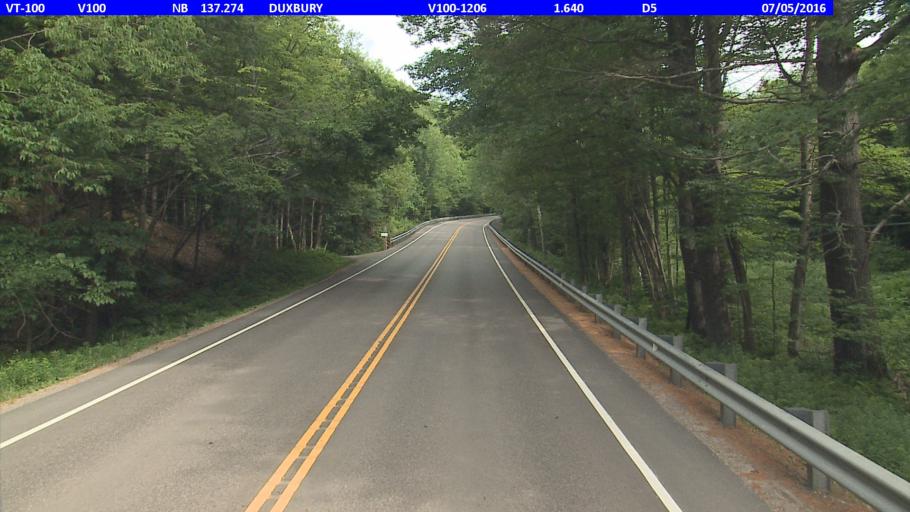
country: US
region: Vermont
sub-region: Washington County
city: Waterbury
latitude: 44.2695
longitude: -72.7852
